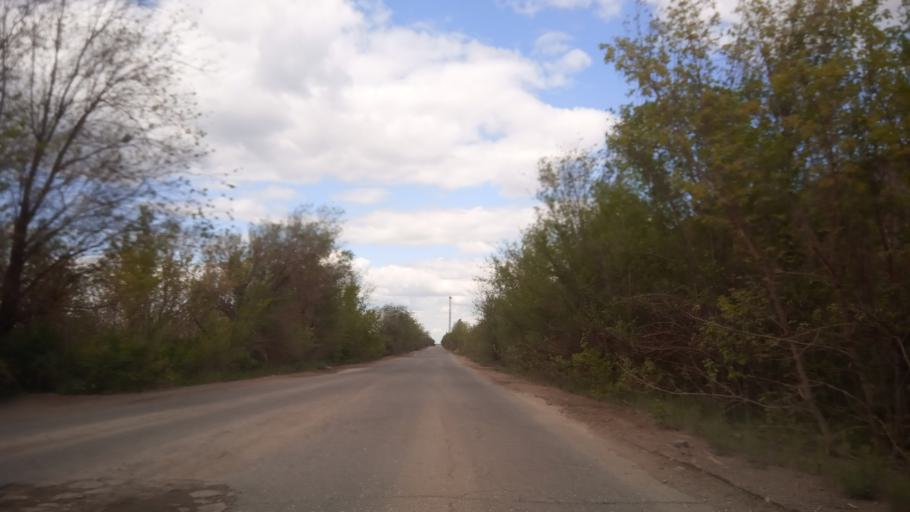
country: RU
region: Orenburg
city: Novotroitsk
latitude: 51.2450
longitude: 58.3591
